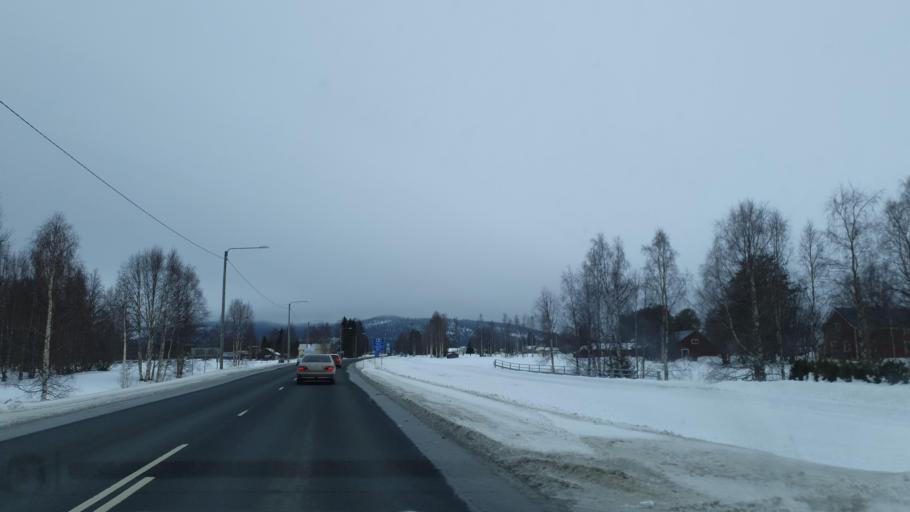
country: FI
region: Lapland
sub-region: Torniolaakso
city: Pello
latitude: 66.5598
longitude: 23.8678
